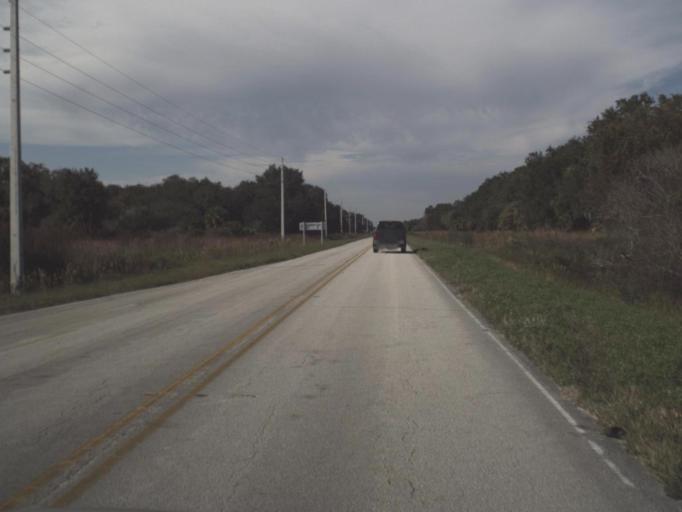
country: US
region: Florida
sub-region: Brevard County
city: Titusville
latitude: 28.6436
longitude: -80.7311
